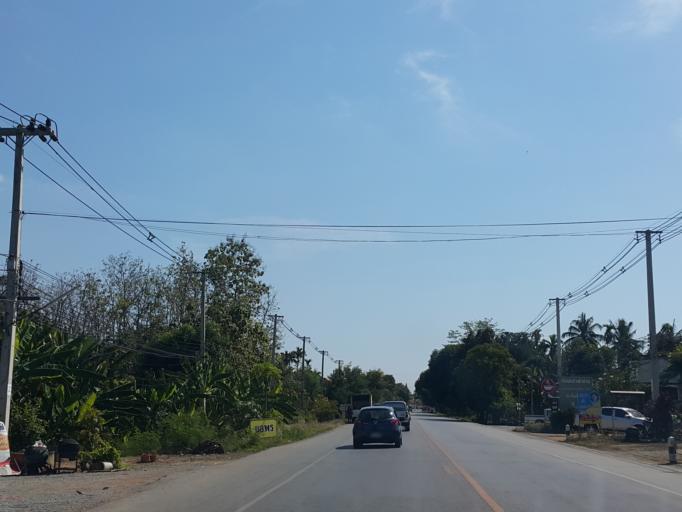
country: TH
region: Sukhothai
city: Sawankhalok
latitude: 17.2907
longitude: 99.8394
